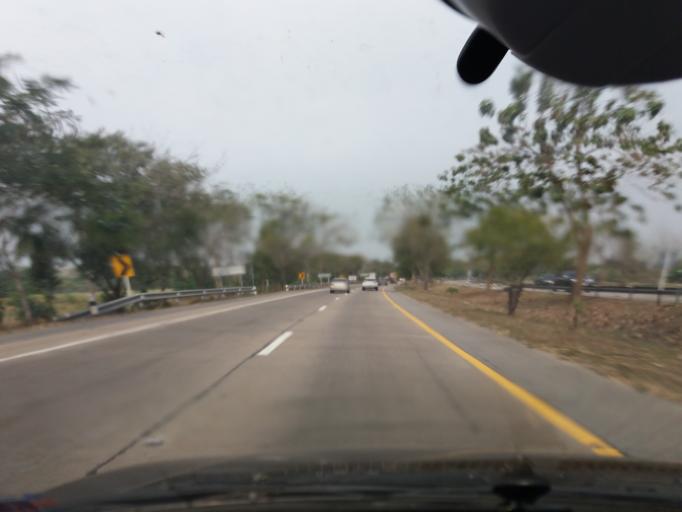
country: TH
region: Suphan Buri
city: Ban Sam Chuk
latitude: 14.7095
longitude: 100.1025
